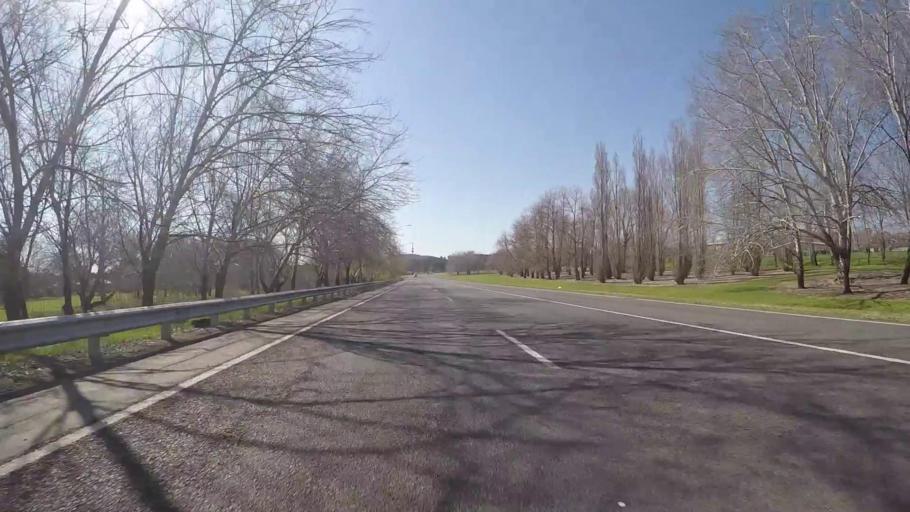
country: AU
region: Australian Capital Territory
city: Forrest
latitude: -35.3213
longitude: 149.0886
